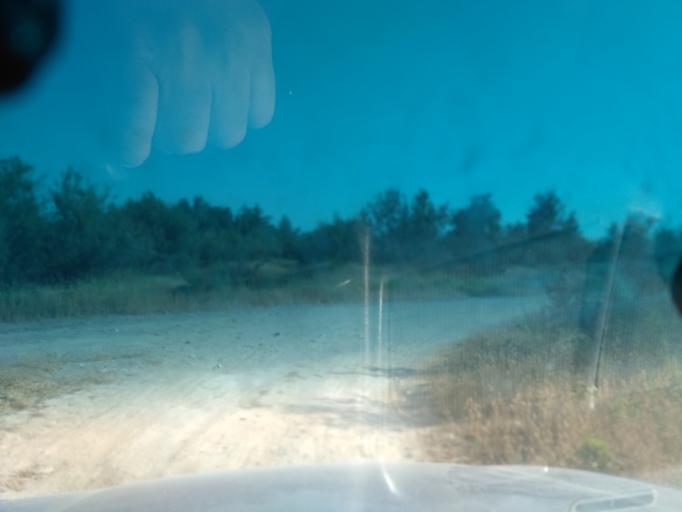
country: TJ
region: Viloyati Sughd
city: Buston
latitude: 40.5587
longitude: 69.0763
